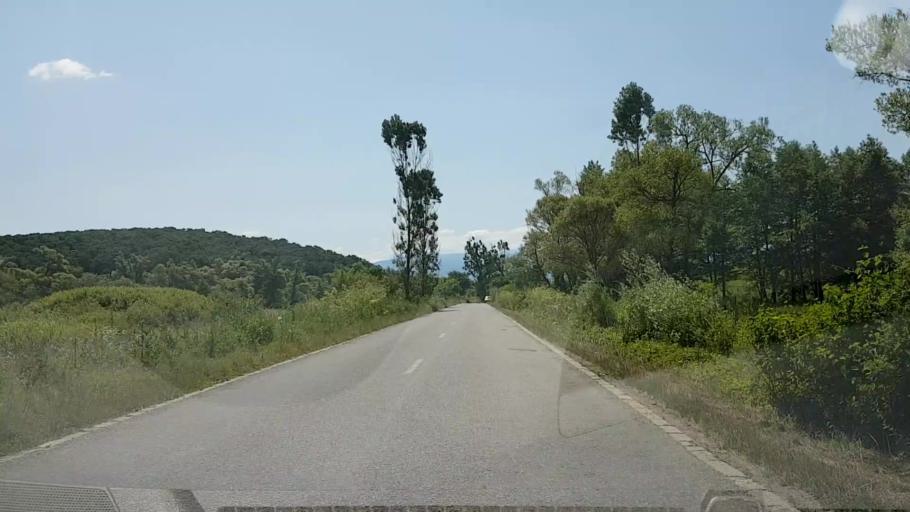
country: RO
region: Brasov
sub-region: Comuna Voila
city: Voila
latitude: 45.8544
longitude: 24.8305
